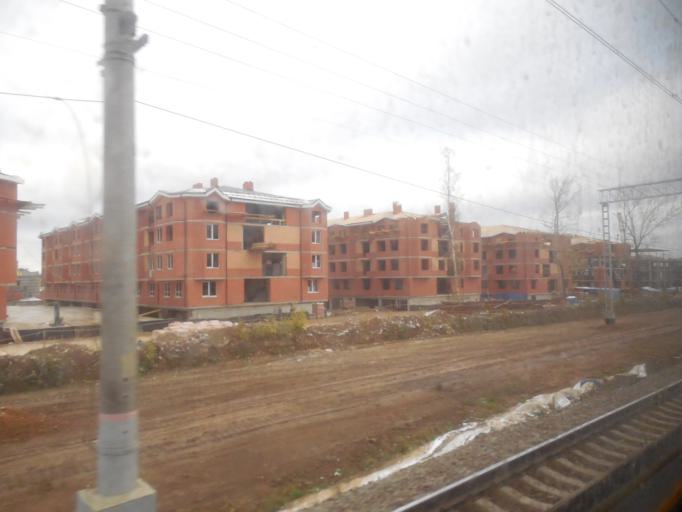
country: RU
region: Moskovskaya
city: Novoivanovskoye
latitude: 55.7100
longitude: 37.3583
